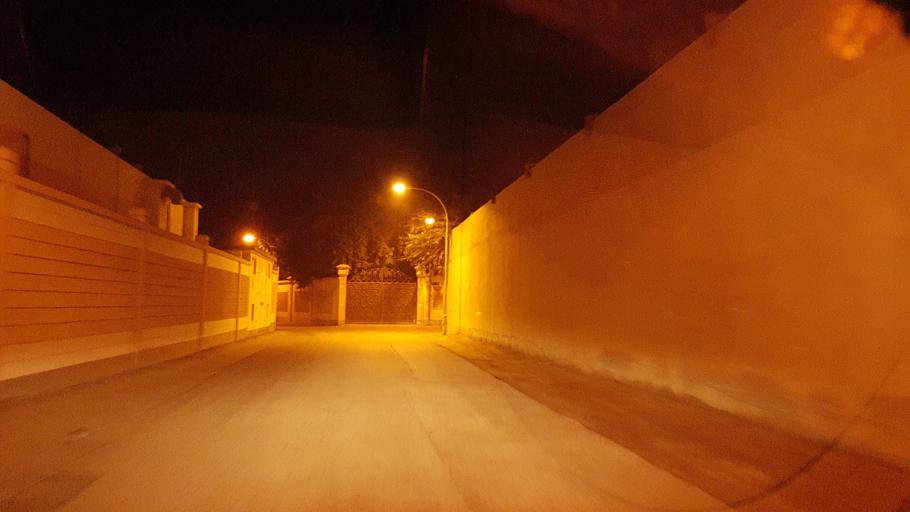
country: BH
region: Manama
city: Jidd Hafs
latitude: 26.2212
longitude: 50.4938
